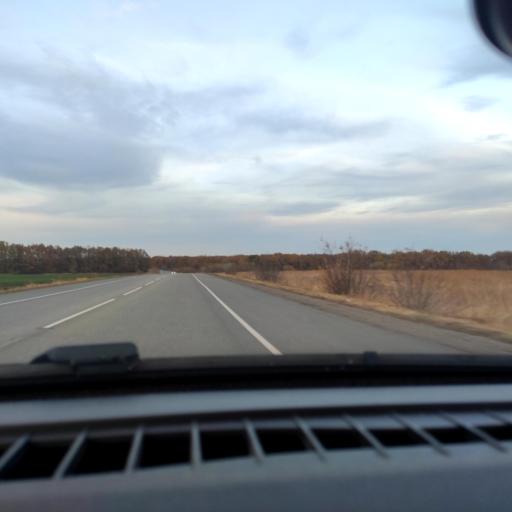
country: RU
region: Voronezj
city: Devitsa
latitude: 51.6070
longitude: 38.9756
